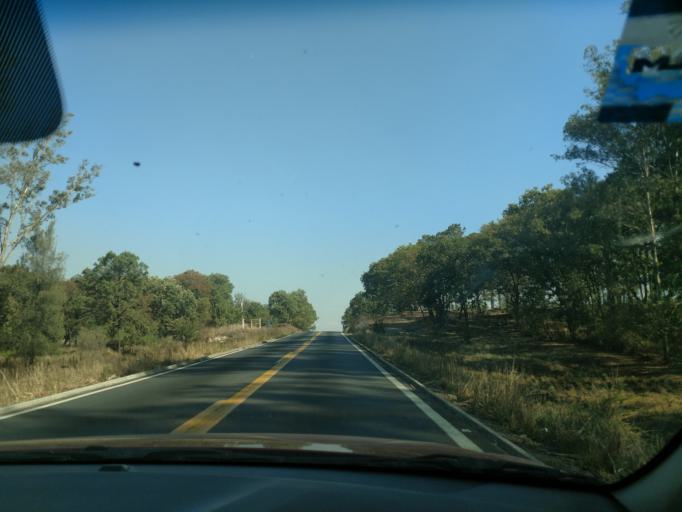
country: MX
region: Nayarit
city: Santa Maria del Oro
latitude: 21.2725
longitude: -104.6481
